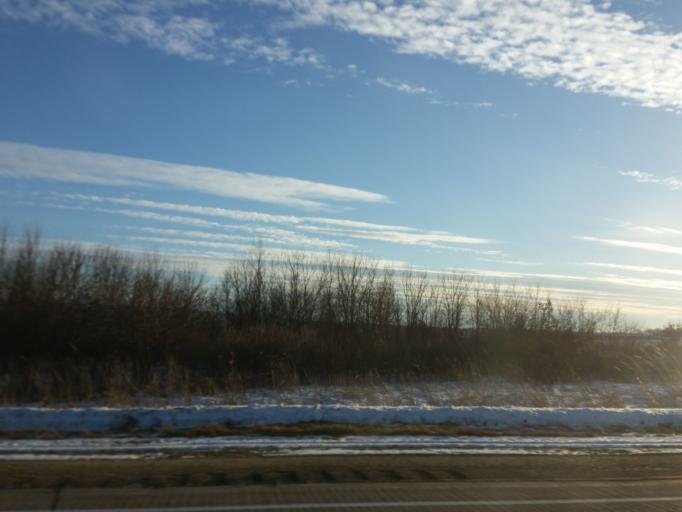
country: US
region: Iowa
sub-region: Butler County
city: Allison
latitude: 42.7449
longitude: -92.8537
